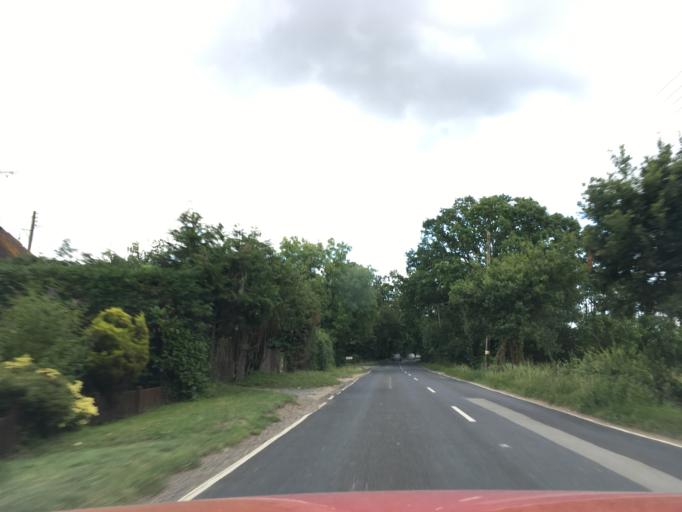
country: GB
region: England
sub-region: Kent
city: Yalding
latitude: 51.2064
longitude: 0.4429
